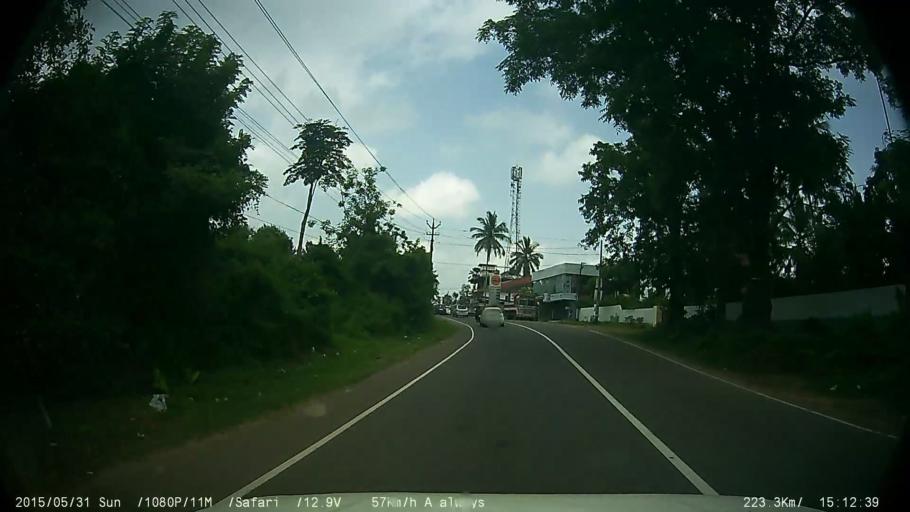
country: IN
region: Kerala
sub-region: Wayanad
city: Panamaram
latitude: 11.6614
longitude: 76.2392
